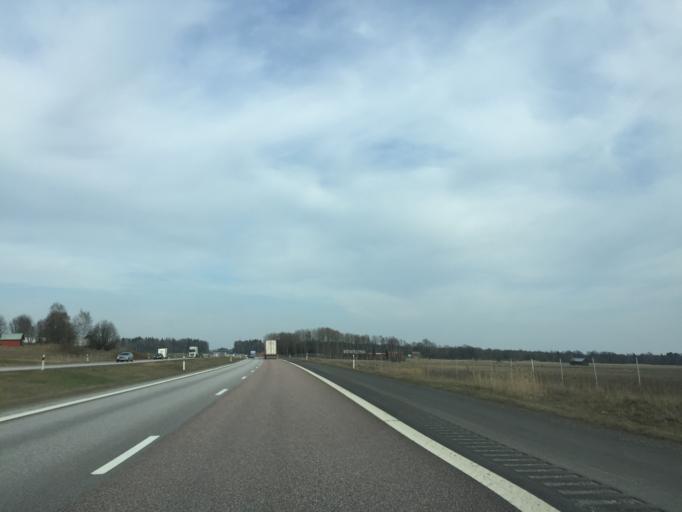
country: SE
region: OErebro
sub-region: Orebro Kommun
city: Hovsta
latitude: 59.3064
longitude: 15.3704
